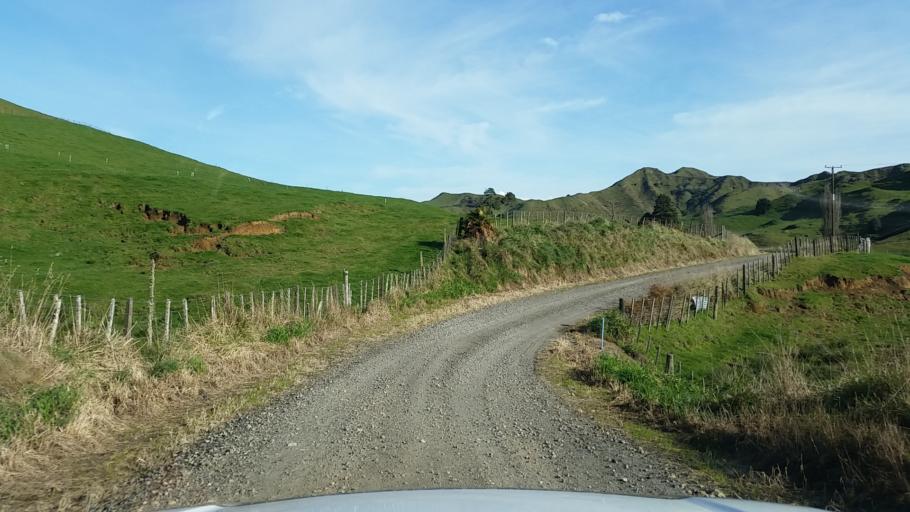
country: NZ
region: Taranaki
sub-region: South Taranaki District
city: Eltham
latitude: -39.3111
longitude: 174.5469
